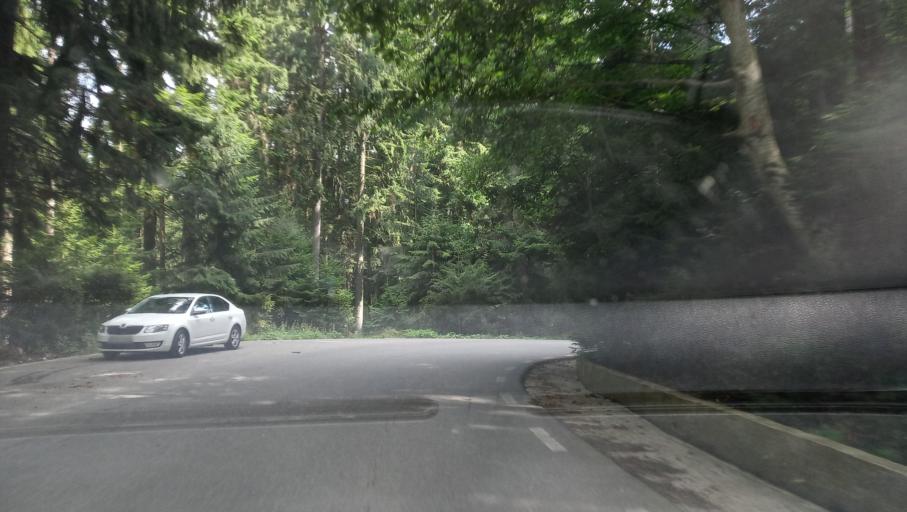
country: RO
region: Prahova
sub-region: Oras Sinaia
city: Sinaia
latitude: 45.3184
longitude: 25.5173
